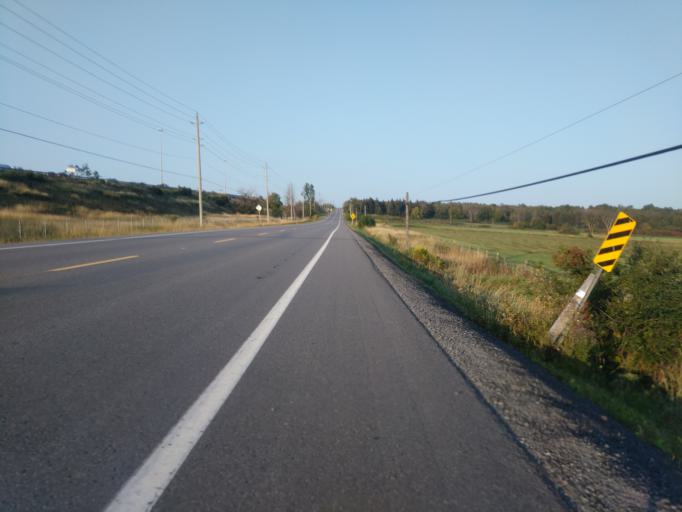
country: CA
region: Ontario
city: Bells Corners
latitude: 45.3348
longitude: -75.8534
